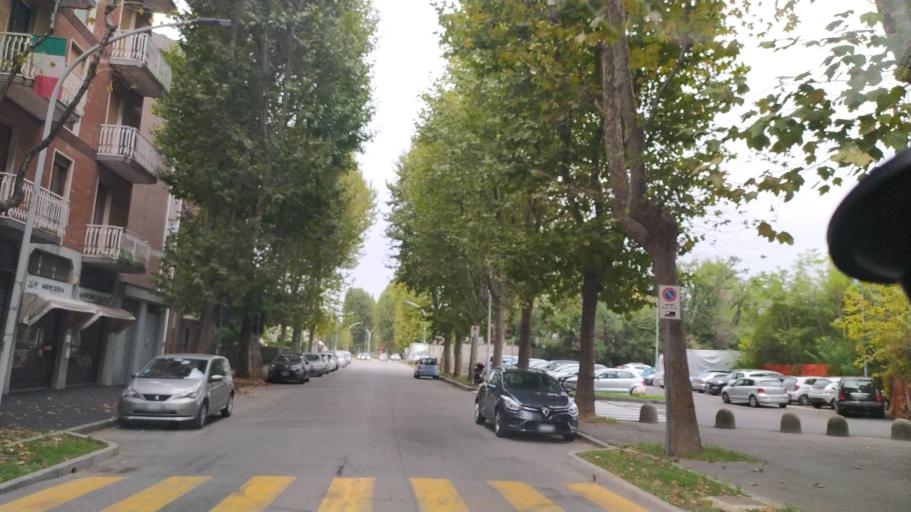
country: IT
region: Lombardy
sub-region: Provincia di Monza e Brianza
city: Seregno
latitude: 45.6409
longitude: 9.2039
